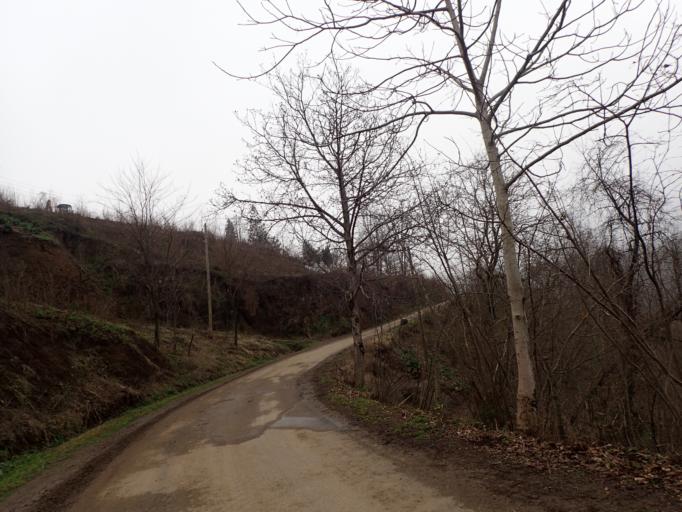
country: TR
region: Ordu
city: Camas
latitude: 40.9225
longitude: 37.5583
